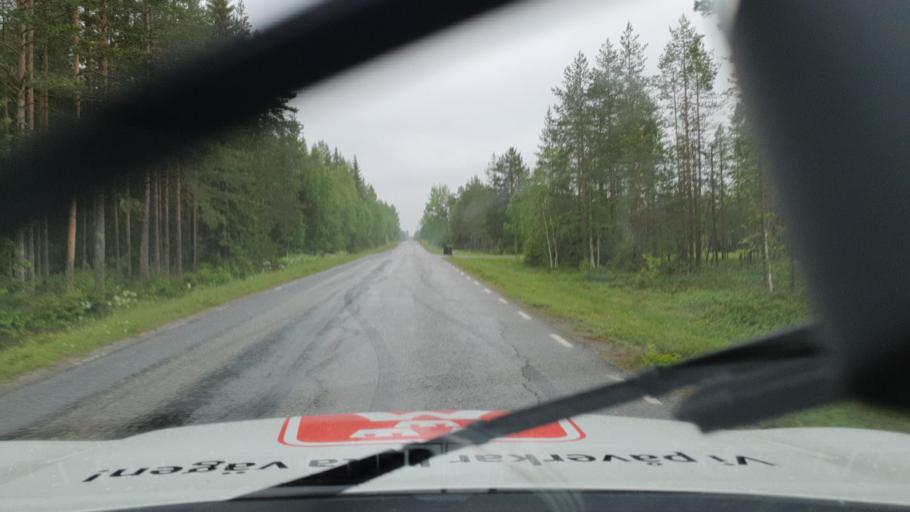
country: SE
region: Vaesterbotten
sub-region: Nordmalings Kommun
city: Nordmaling
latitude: 63.8165
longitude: 19.4967
